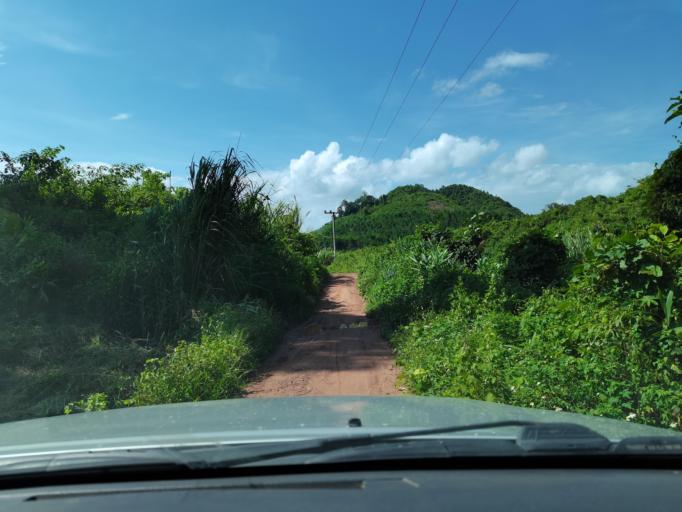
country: LA
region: Loungnamtha
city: Muang Nale
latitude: 20.5607
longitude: 101.0590
